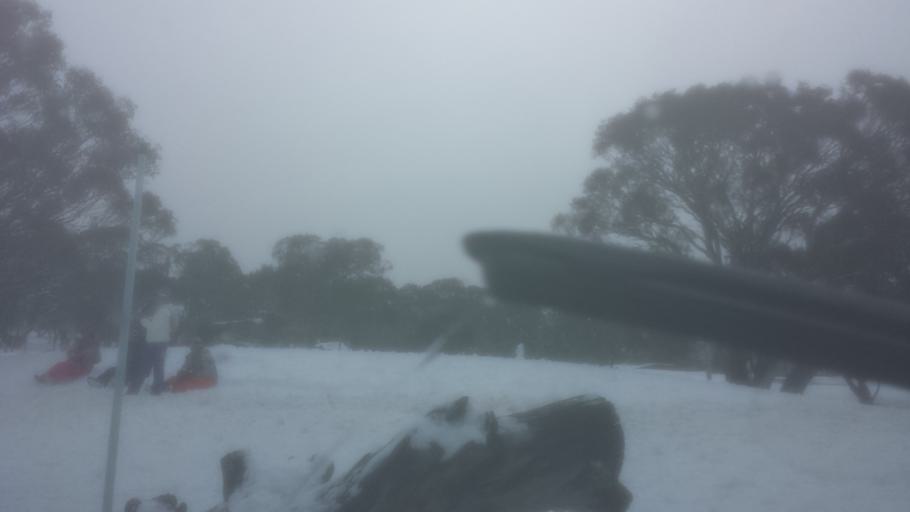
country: AU
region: Victoria
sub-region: Alpine
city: Mount Beauty
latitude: -37.0227
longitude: 147.2391
